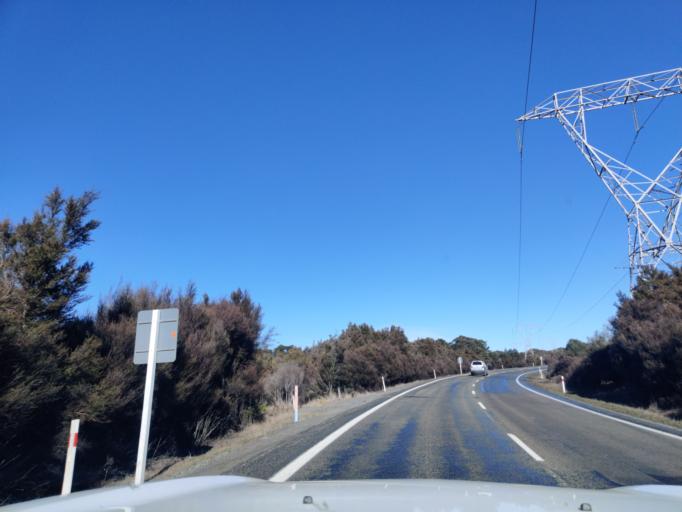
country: NZ
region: Waikato
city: Turangi
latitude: -39.2030
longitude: 175.7568
